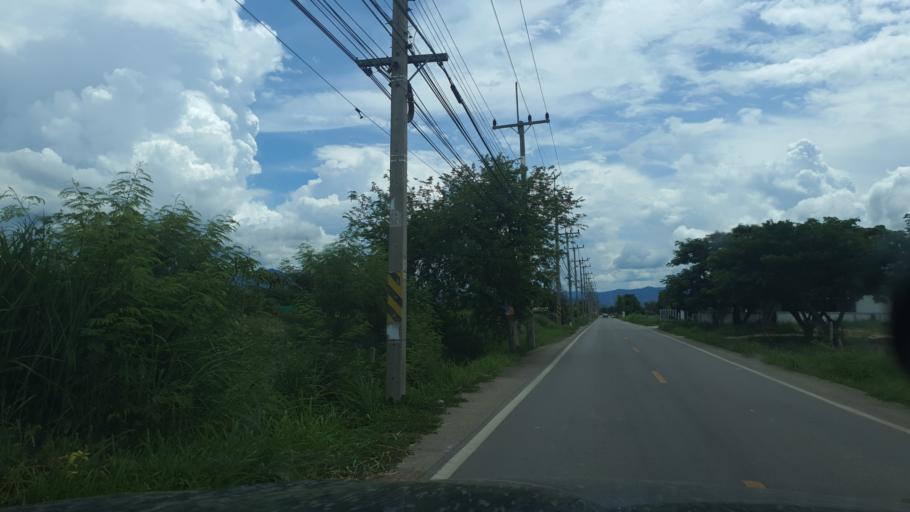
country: TH
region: Lampang
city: Sop Prap
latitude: 17.8829
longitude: 99.3777
